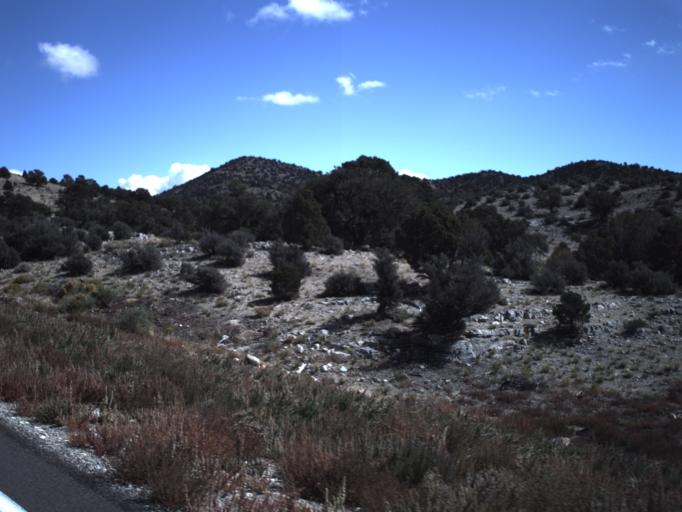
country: US
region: Utah
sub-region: Beaver County
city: Milford
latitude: 38.5153
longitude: -113.5605
